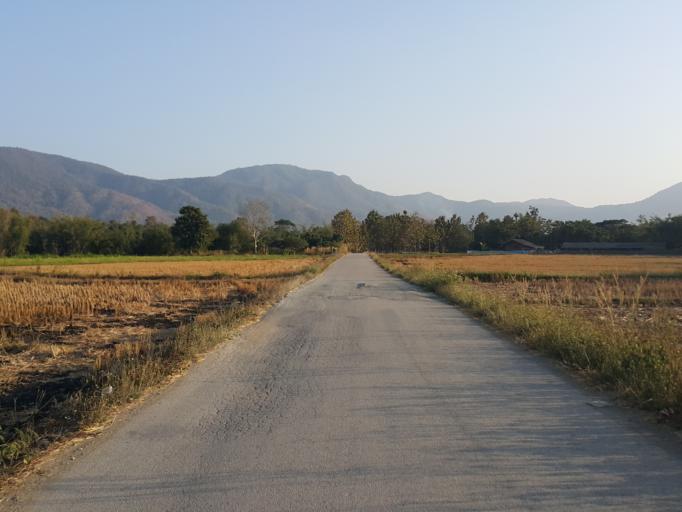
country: TH
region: Chiang Mai
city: Mae On
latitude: 18.7782
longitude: 99.2563
